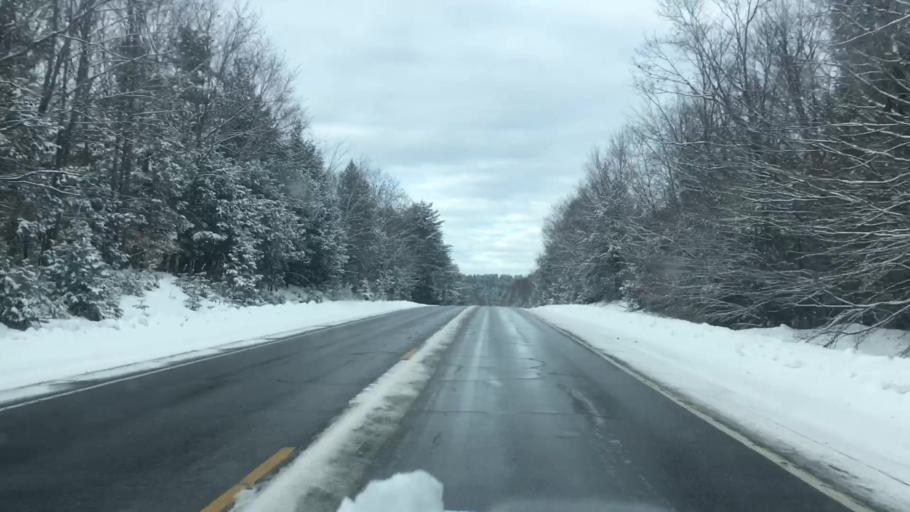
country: US
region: Maine
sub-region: Cumberland County
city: Bridgton
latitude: 44.0033
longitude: -70.6675
